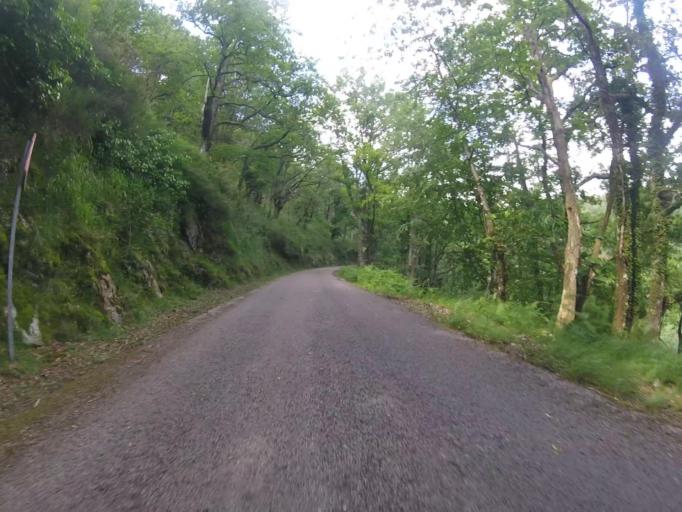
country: ES
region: Navarre
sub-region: Provincia de Navarra
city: Goizueta
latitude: 43.2197
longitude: -1.8076
